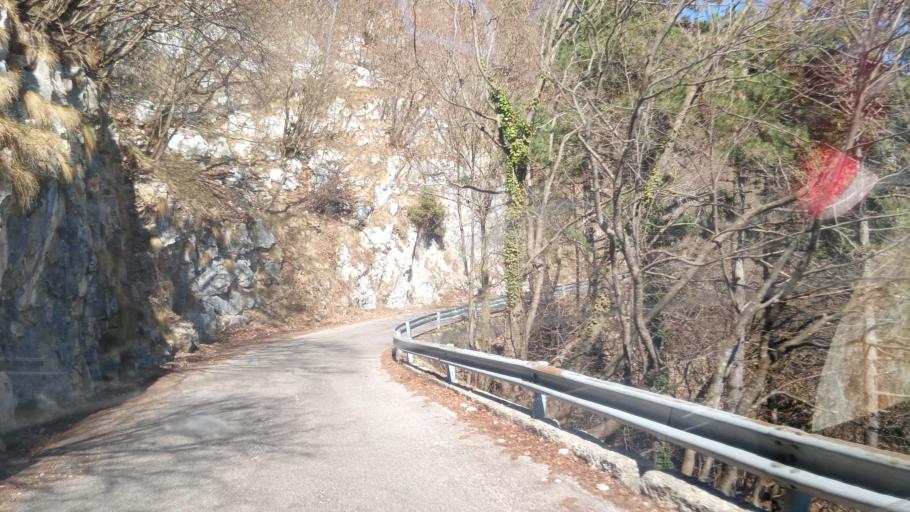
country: IT
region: Veneto
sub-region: Provincia di Treviso
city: Borso del Grappa
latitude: 45.8318
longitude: 11.7751
